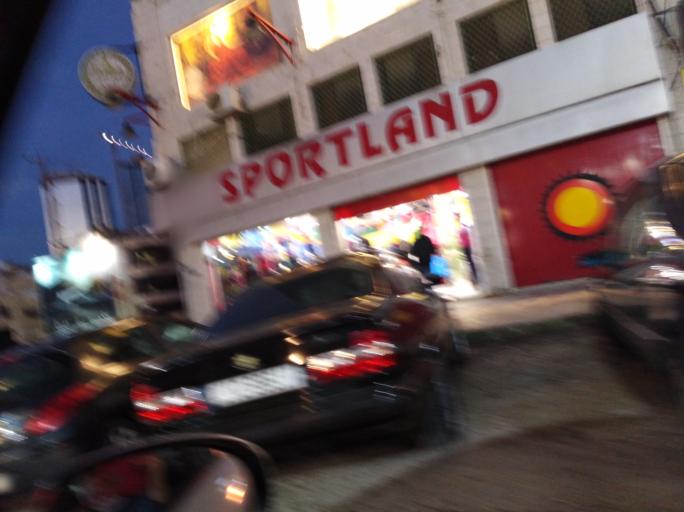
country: JO
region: Amman
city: Wadi as Sir
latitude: 31.9573
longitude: 35.8653
